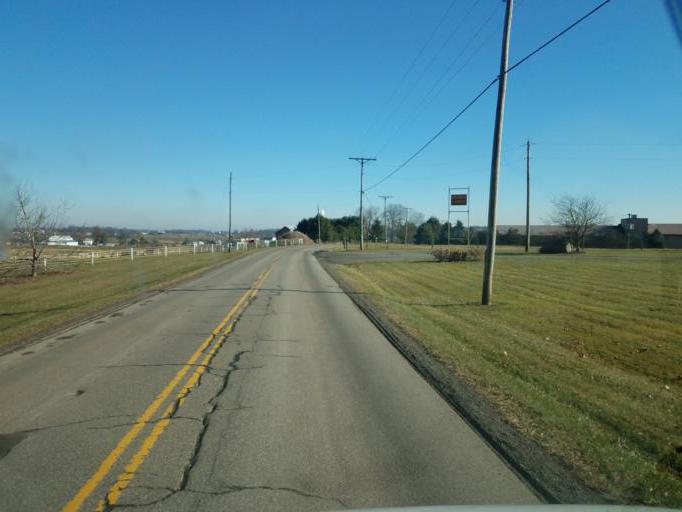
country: US
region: Ohio
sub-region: Wayne County
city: Apple Creek
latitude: 40.6970
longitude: -81.8017
